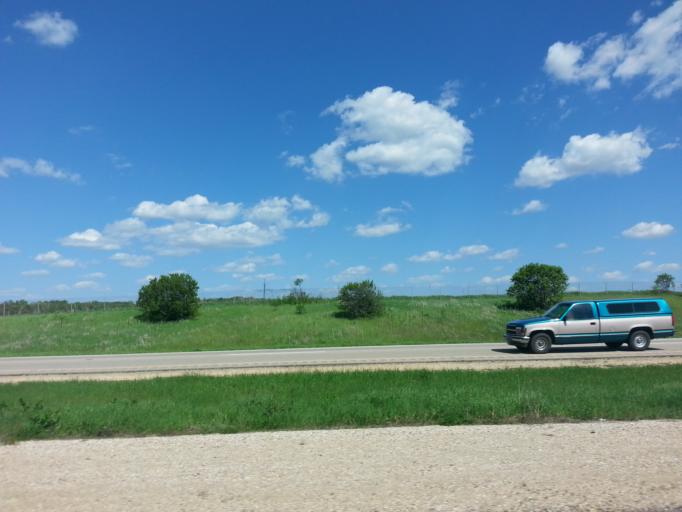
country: US
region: Wisconsin
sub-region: Rock County
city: Beloit
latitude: 42.5328
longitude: -88.9752
